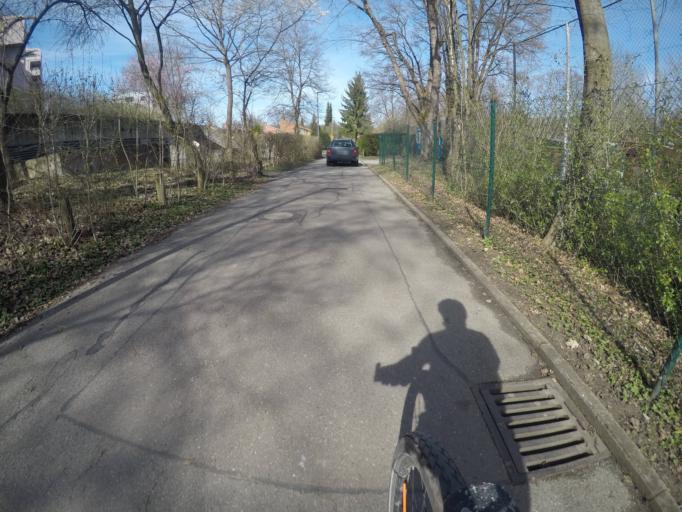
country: DE
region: Baden-Wuerttemberg
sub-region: Regierungsbezirk Stuttgart
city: Korntal
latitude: 48.8114
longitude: 9.1266
